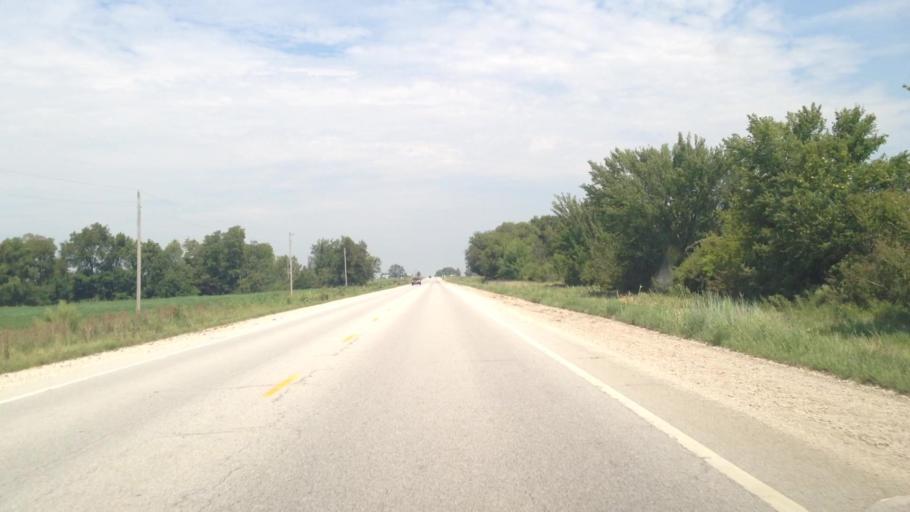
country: US
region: Kansas
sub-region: Neosho County
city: Erie
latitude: 37.4652
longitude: -95.2695
